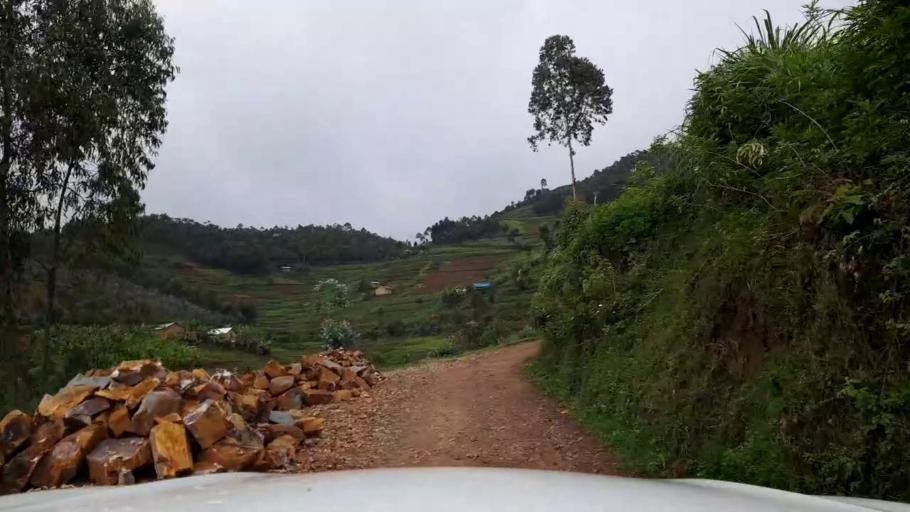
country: RW
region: Northern Province
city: Musanze
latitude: -1.6042
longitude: 29.7675
